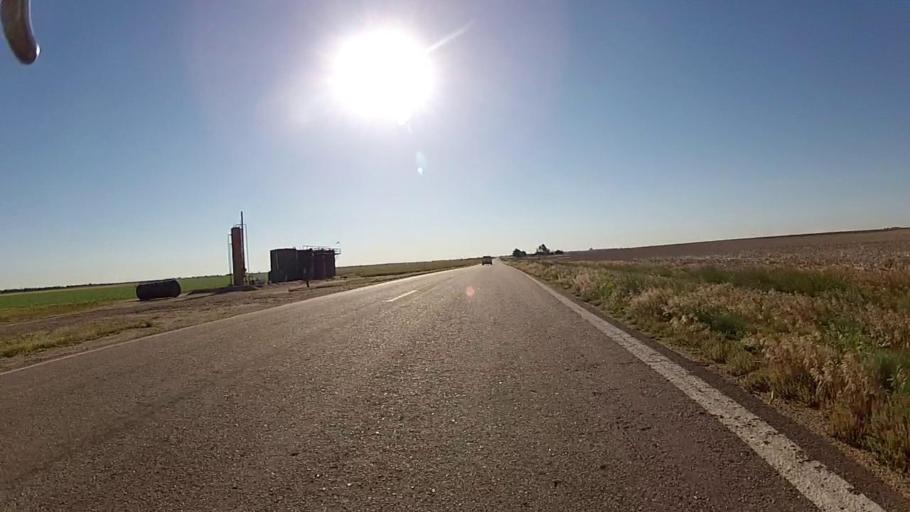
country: US
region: Kansas
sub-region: Ford County
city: Dodge City
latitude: 37.6461
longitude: -99.8212
